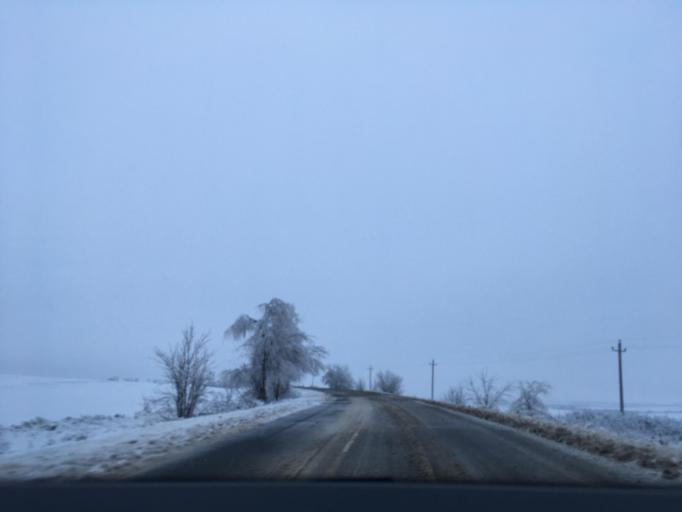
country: RU
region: Voronezj
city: Verkhniy Mamon
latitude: 50.0241
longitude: 40.0751
